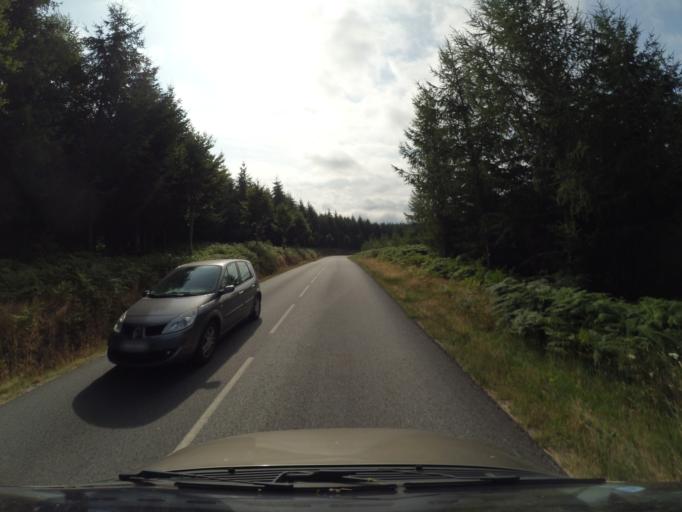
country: FR
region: Limousin
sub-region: Departement de la Correze
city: Meymac
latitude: 45.5988
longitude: 2.1248
